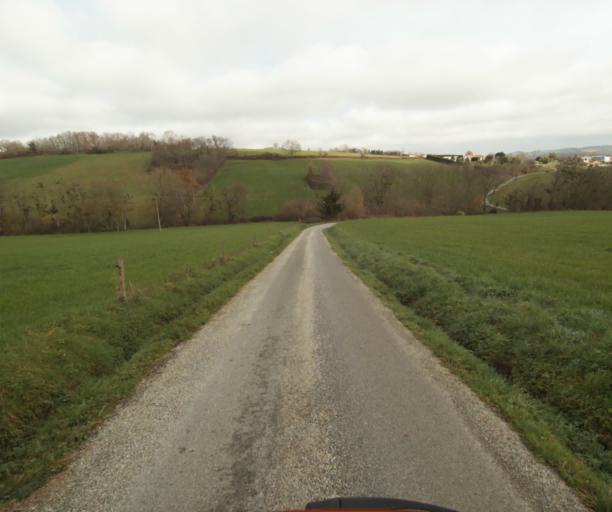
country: FR
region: Midi-Pyrenees
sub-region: Departement de l'Ariege
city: Pamiers
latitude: 43.1064
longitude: 1.5154
